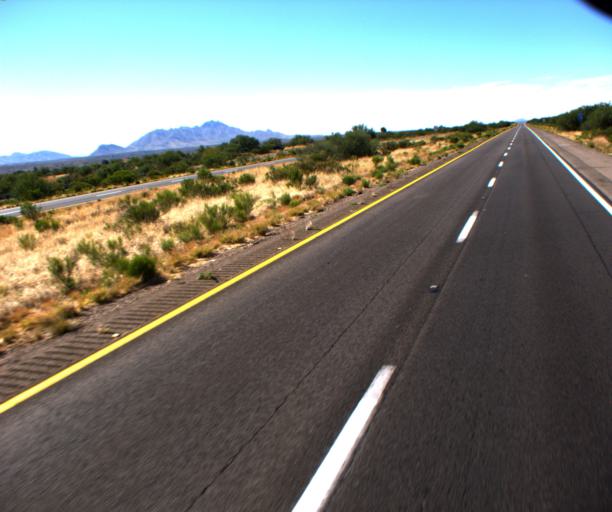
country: US
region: Arizona
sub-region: Santa Cruz County
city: Tubac
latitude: 31.6452
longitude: -111.0584
